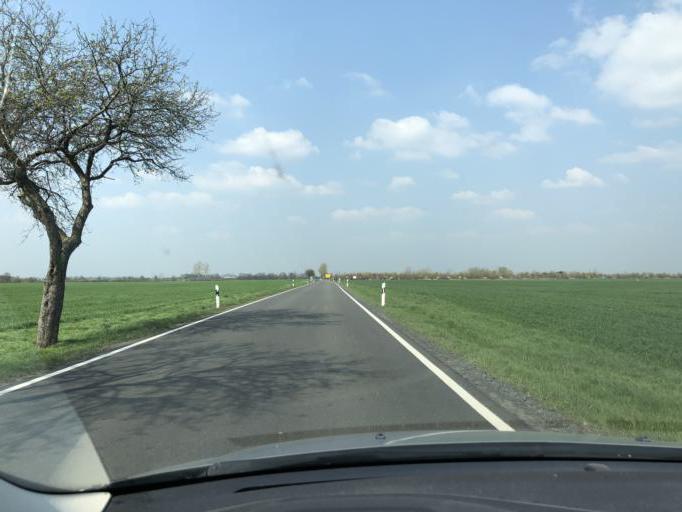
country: DE
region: Saxony
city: Wiedemar
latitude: 51.4917
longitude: 12.2136
